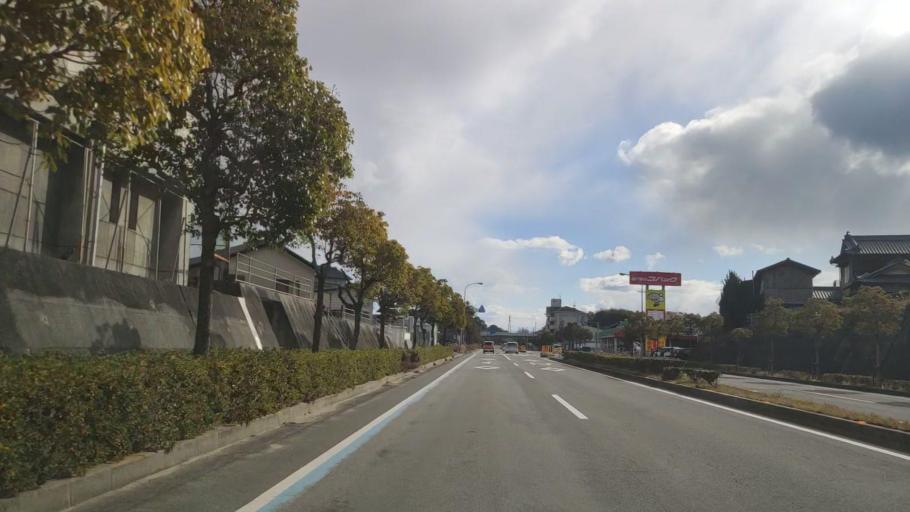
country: JP
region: Ehime
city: Hojo
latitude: 34.0597
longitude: 132.9678
